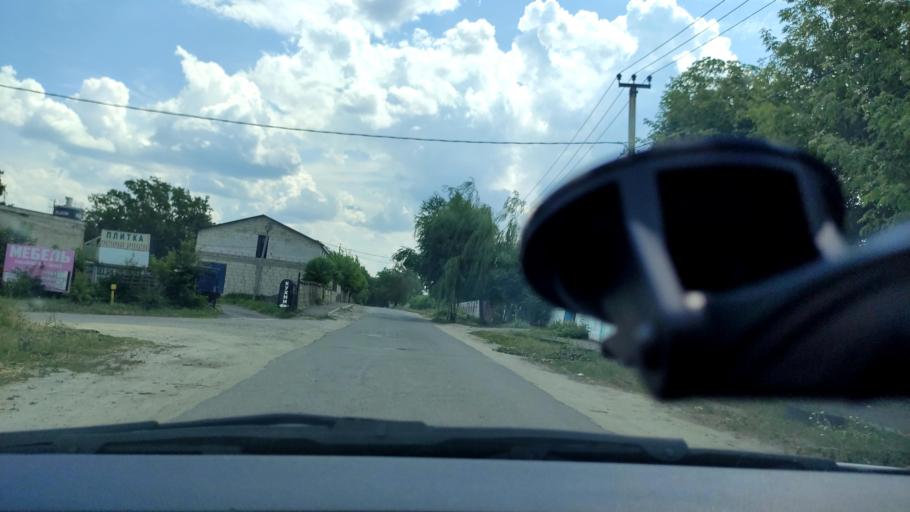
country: RU
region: Voronezj
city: Ramon'
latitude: 51.9035
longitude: 39.3331
